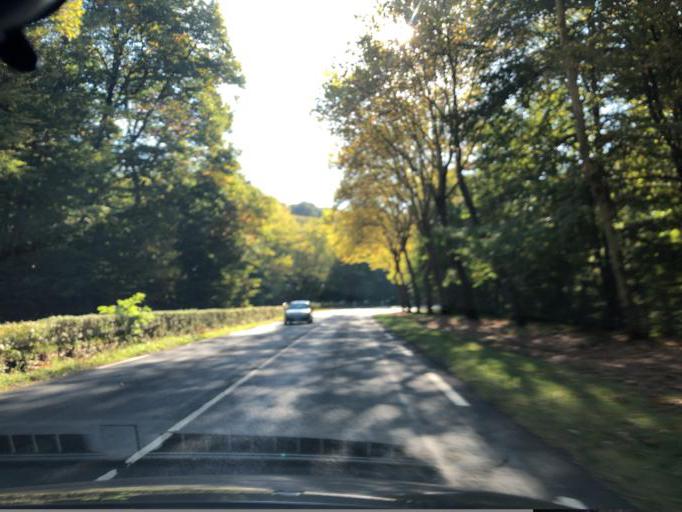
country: FR
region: Ile-de-France
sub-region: Departement des Yvelines
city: Rambouillet
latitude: 48.6600
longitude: 1.8185
